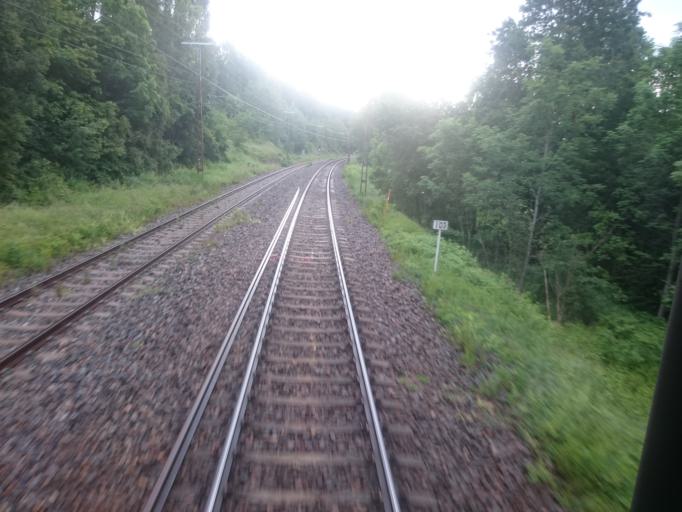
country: SE
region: OEstergoetland
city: Lindo
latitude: 58.6672
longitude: 16.2646
